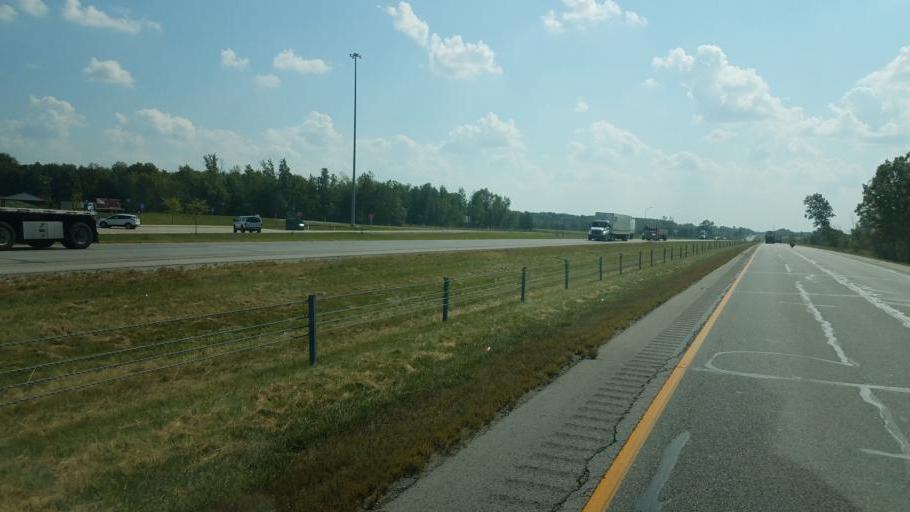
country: US
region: Indiana
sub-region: DeKalb County
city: Garrett
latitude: 41.2965
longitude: -85.0875
